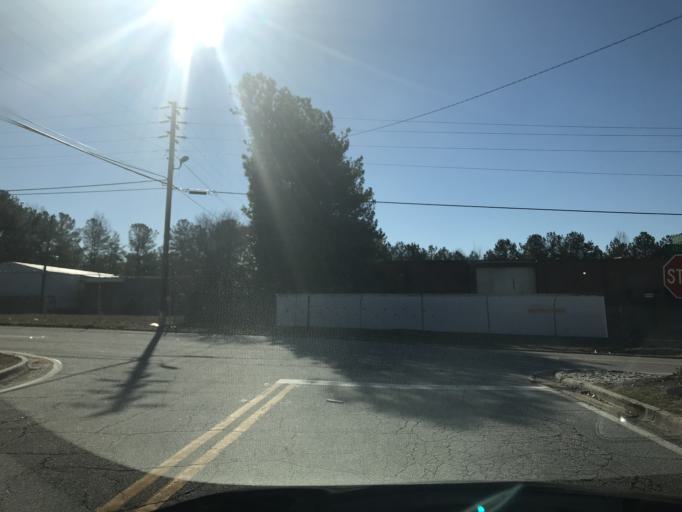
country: US
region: Georgia
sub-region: Clayton County
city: Morrow
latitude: 33.5699
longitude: -84.3556
